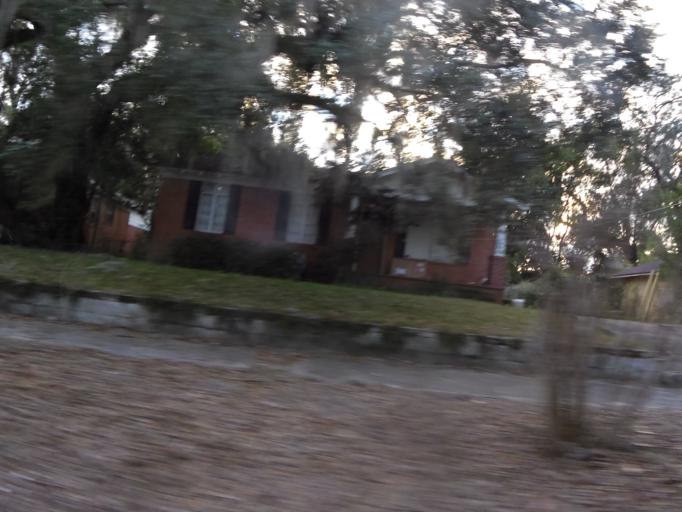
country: US
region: Florida
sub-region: Duval County
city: Jacksonville
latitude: 30.2917
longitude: -81.7117
